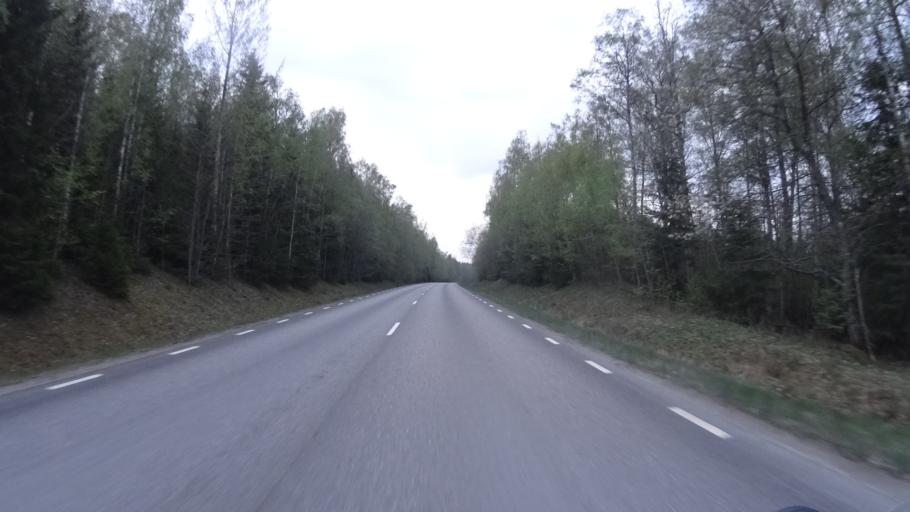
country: SE
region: Vaestra Goetaland
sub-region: Gotene Kommun
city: Goetene
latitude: 58.6101
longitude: 13.4010
